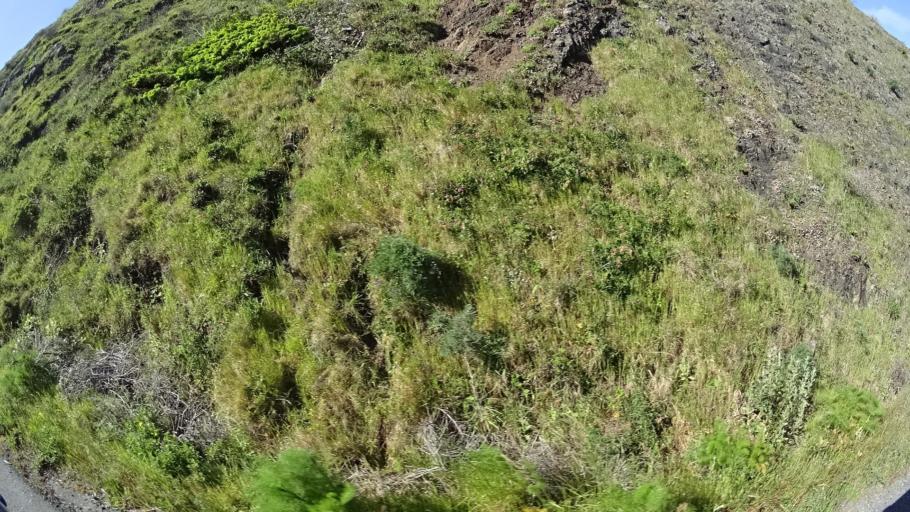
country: US
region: California
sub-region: Humboldt County
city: Ferndale
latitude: 40.3516
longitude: -124.3597
